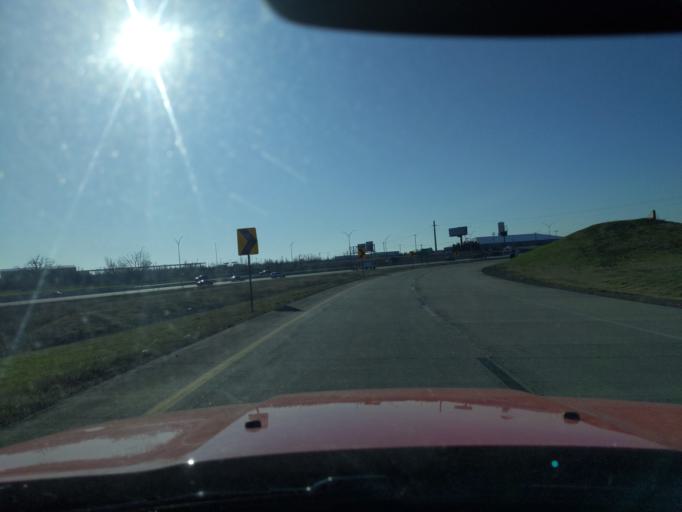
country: US
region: Oklahoma
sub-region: Cleveland County
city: Moore
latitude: 35.3909
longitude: -97.4968
